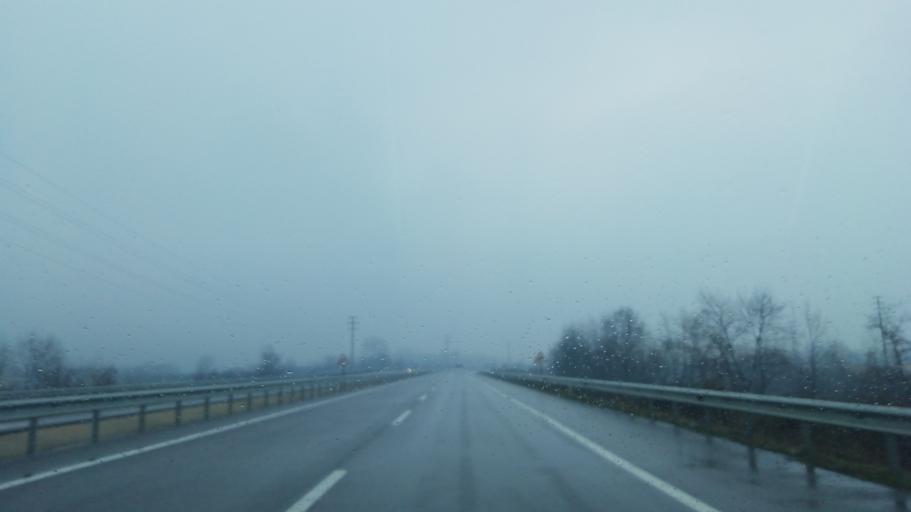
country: TR
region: Sakarya
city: Akyazi
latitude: 40.6474
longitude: 30.6082
